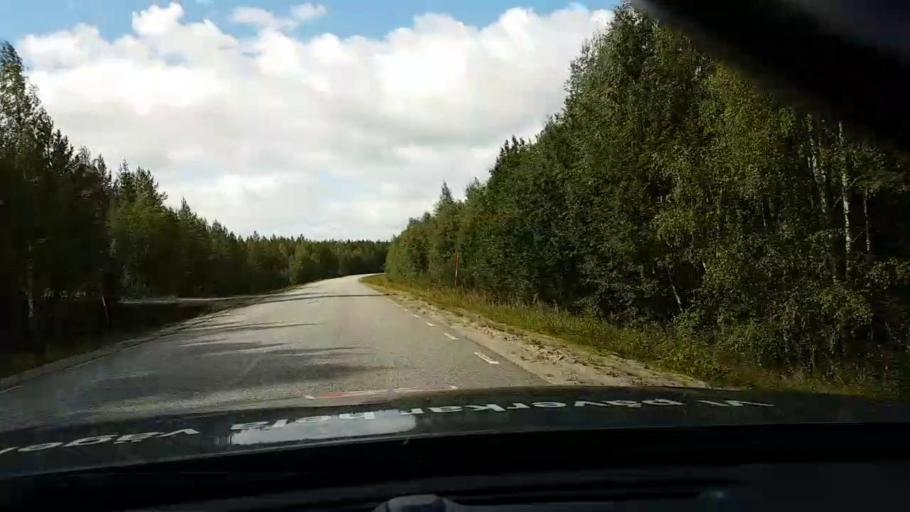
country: SE
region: Vaesterbotten
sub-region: Asele Kommun
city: Asele
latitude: 63.9300
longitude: 17.3017
